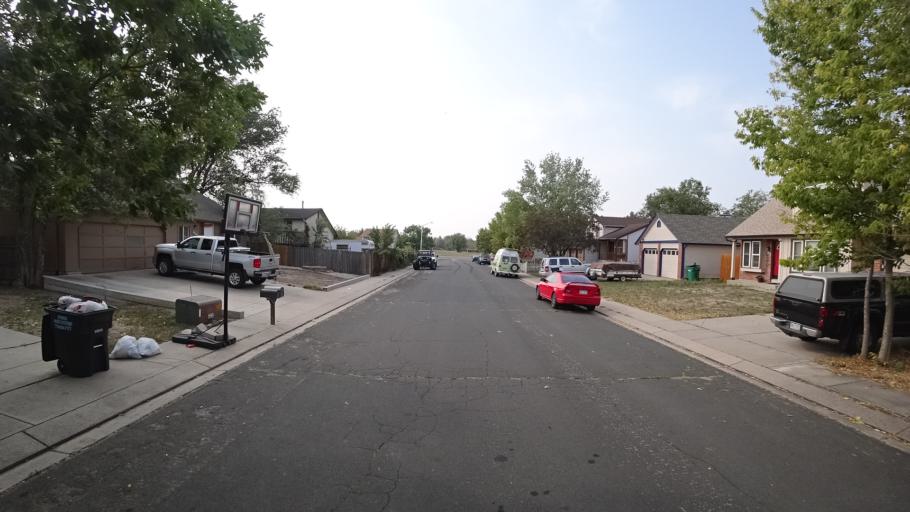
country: US
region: Colorado
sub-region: El Paso County
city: Stratmoor
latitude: 38.8060
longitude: -104.7483
